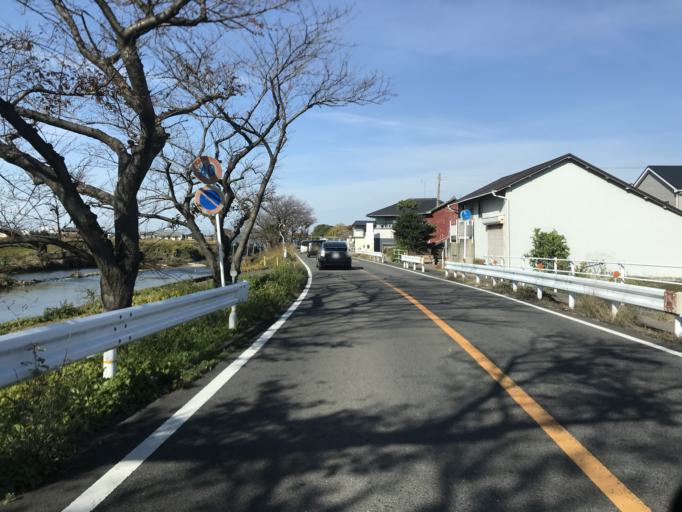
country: JP
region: Aichi
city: Iwakura
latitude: 35.2282
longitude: 136.8462
